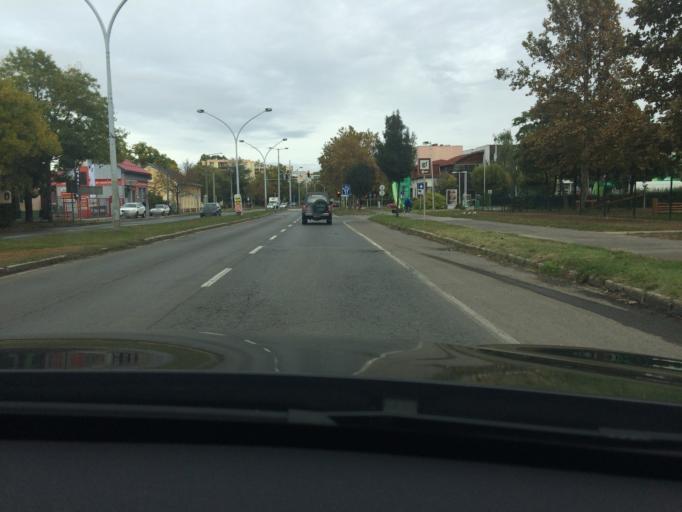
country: HU
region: Szabolcs-Szatmar-Bereg
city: Nyiregyhaza
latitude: 47.9609
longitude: 21.7051
